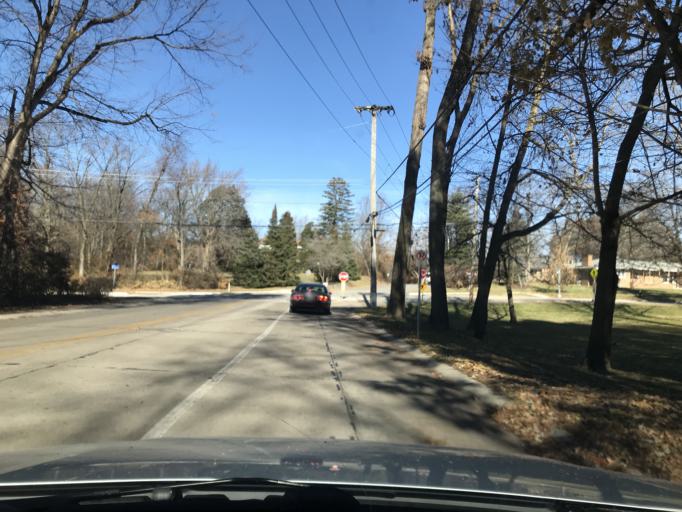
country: US
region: Illinois
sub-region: McDonough County
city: Macomb
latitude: 40.4475
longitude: -90.6708
